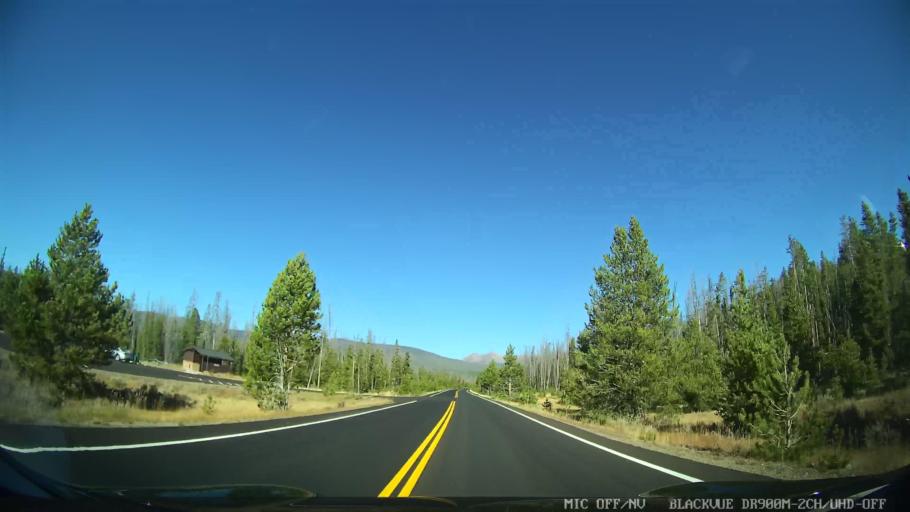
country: US
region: Colorado
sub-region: Grand County
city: Granby
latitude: 40.2819
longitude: -105.8375
